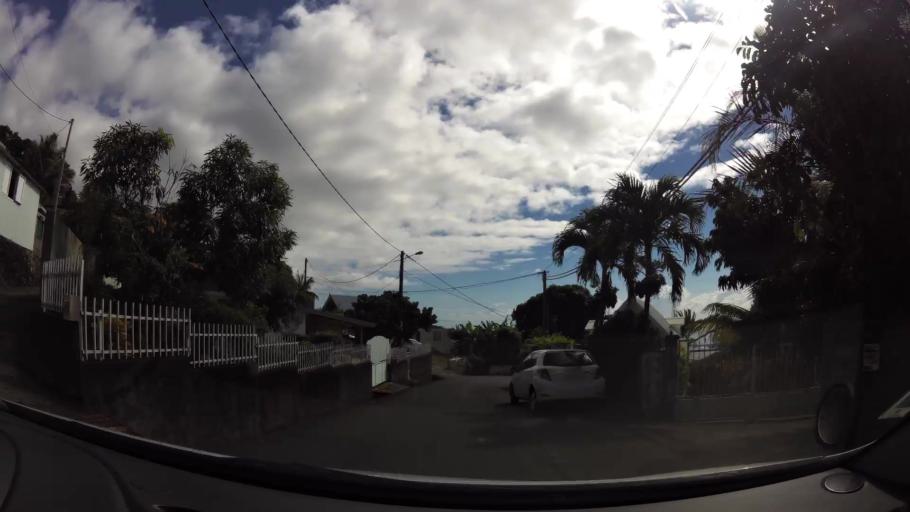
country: RE
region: Reunion
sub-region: Reunion
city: Saint-Denis
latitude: -20.9291
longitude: 55.4895
